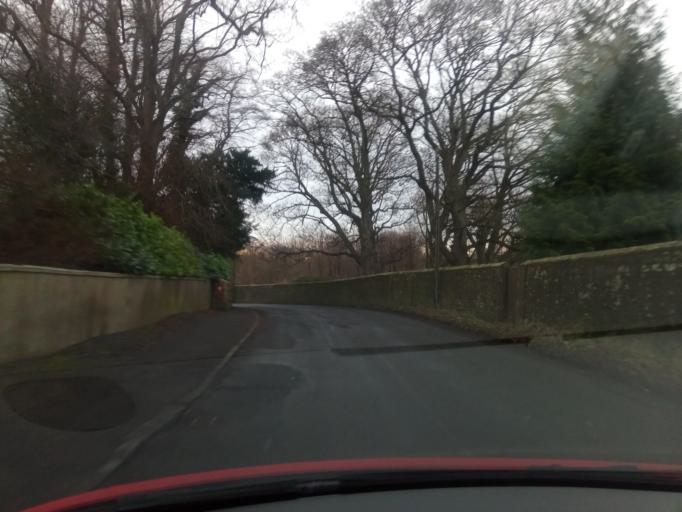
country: GB
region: England
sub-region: Northumberland
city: Alnwick
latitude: 55.4230
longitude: -1.7187
